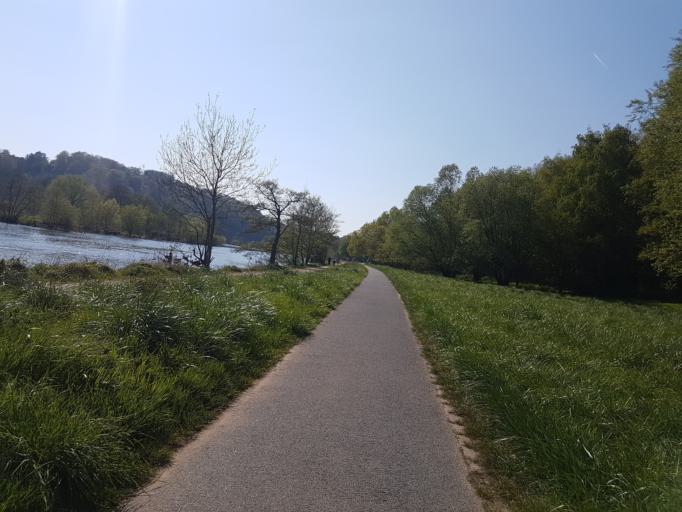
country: DE
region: North Rhine-Westphalia
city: Hattingen
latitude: 51.4128
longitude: 7.2390
